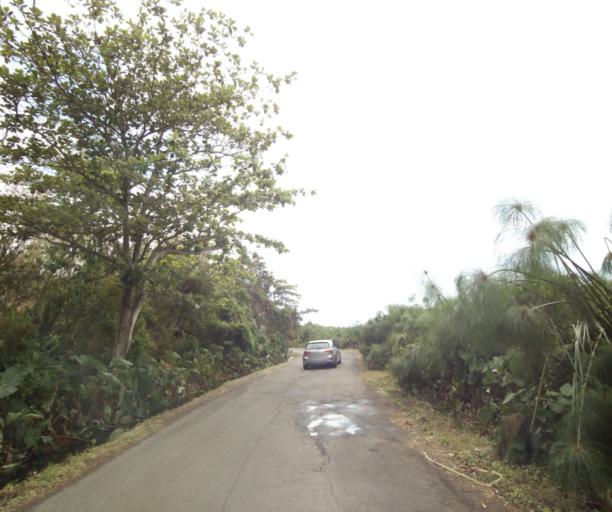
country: RE
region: Reunion
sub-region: Reunion
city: Saint-Paul
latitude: -20.9990
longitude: 55.3026
